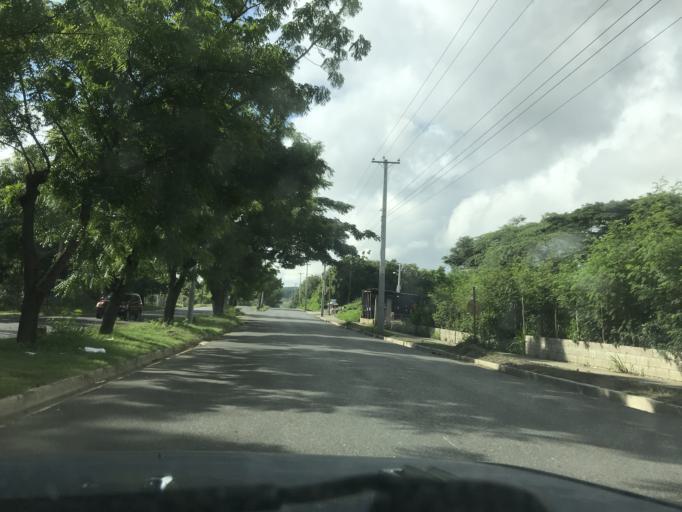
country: DO
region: Santiago
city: Santiago de los Caballeros
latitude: 19.4184
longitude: -70.7336
